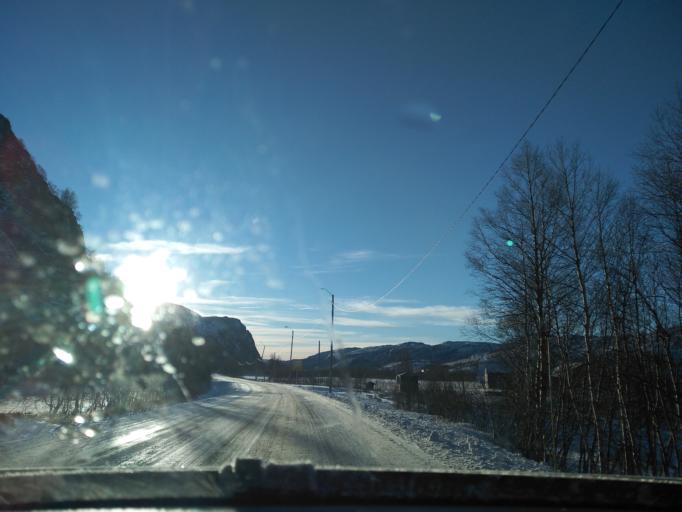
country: NO
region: Vest-Agder
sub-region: Sirdal
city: Tonstad
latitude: 59.0084
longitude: 6.9326
